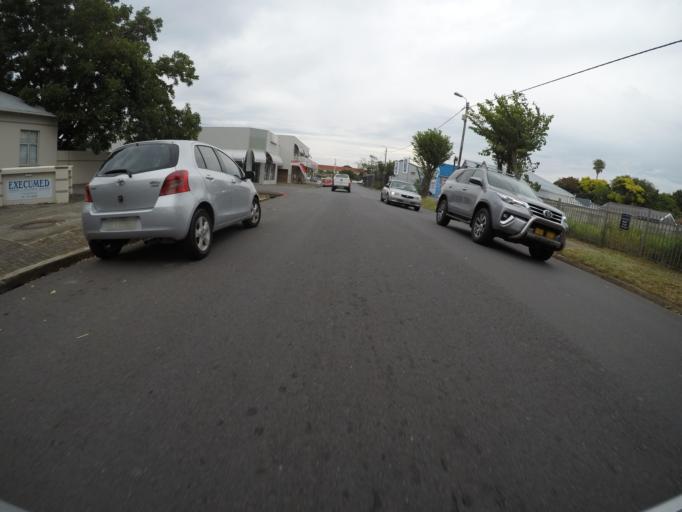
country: ZA
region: Eastern Cape
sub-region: Buffalo City Metropolitan Municipality
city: East London
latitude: -32.9788
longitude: 27.9006
